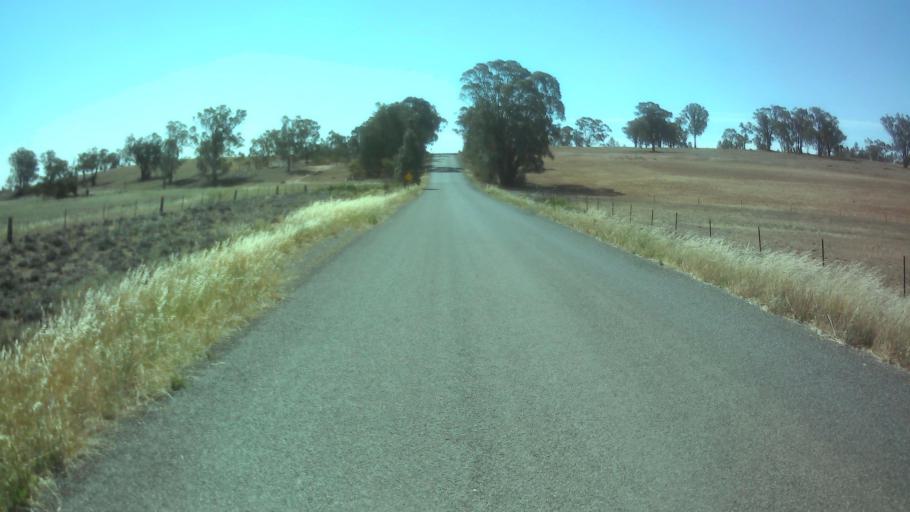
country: AU
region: New South Wales
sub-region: Weddin
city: Grenfell
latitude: -33.7590
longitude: 147.8582
